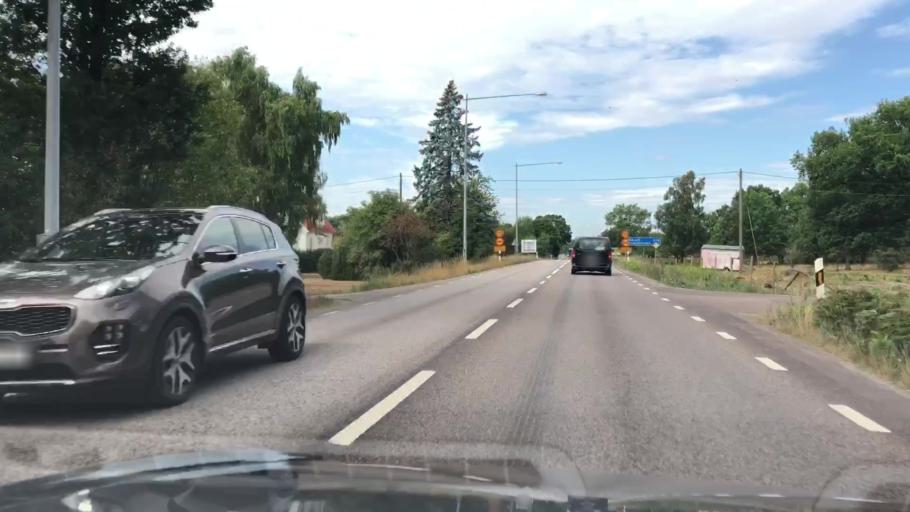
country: SE
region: Blekinge
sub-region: Karlskrona Kommun
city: Jaemjoe
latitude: 56.1856
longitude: 15.7176
